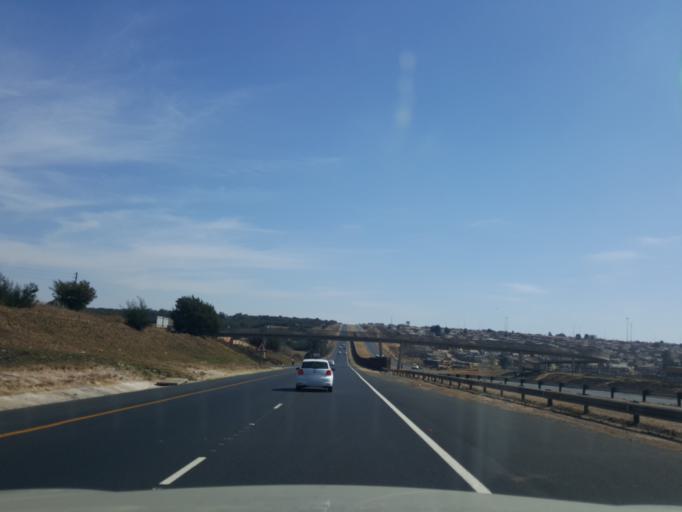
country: ZA
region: Mpumalanga
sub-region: Nkangala District Municipality
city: Witbank
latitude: -25.8742
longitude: 29.1334
